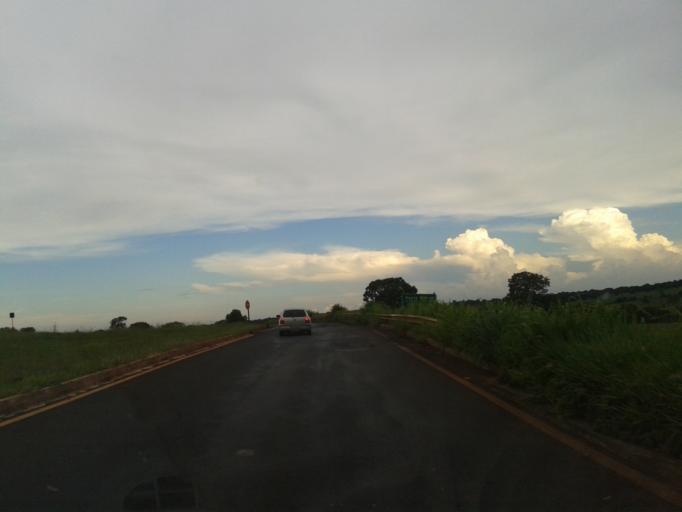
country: BR
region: Minas Gerais
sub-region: Santa Vitoria
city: Santa Vitoria
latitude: -18.8766
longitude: -50.1232
